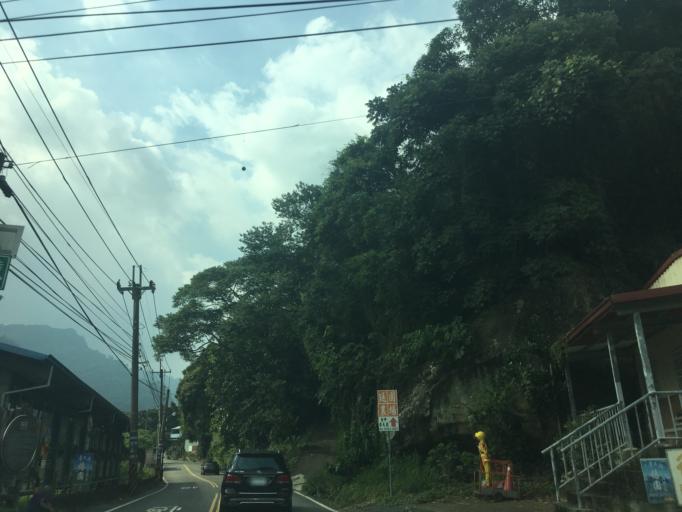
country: TW
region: Taiwan
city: Fengyuan
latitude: 24.3064
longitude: 120.9244
